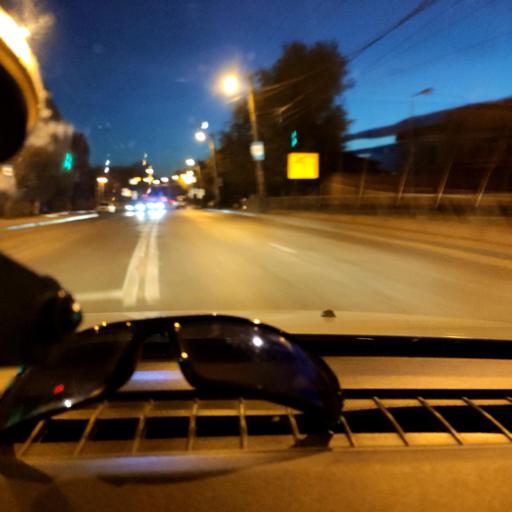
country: RU
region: Samara
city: Rozhdestveno
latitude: 53.1777
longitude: 50.0750
